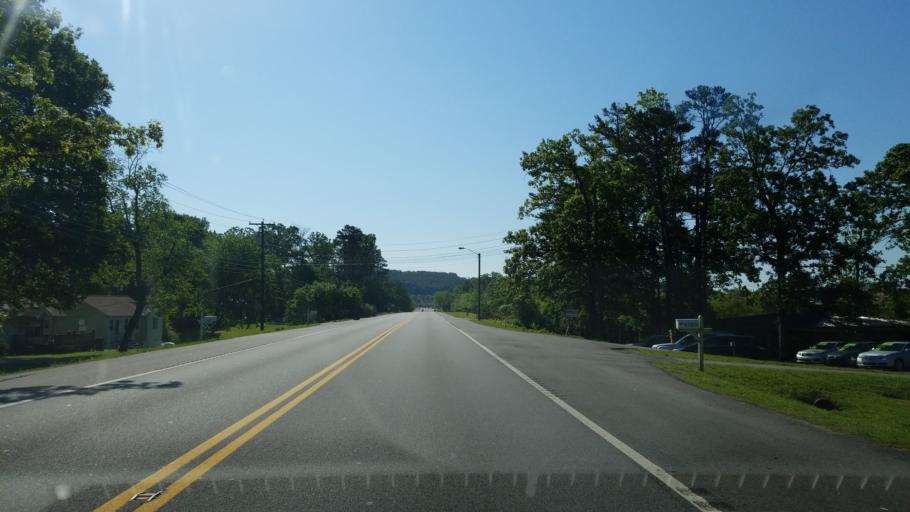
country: US
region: Tennessee
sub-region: Hamilton County
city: Harrison
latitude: 35.0645
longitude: -85.1429
